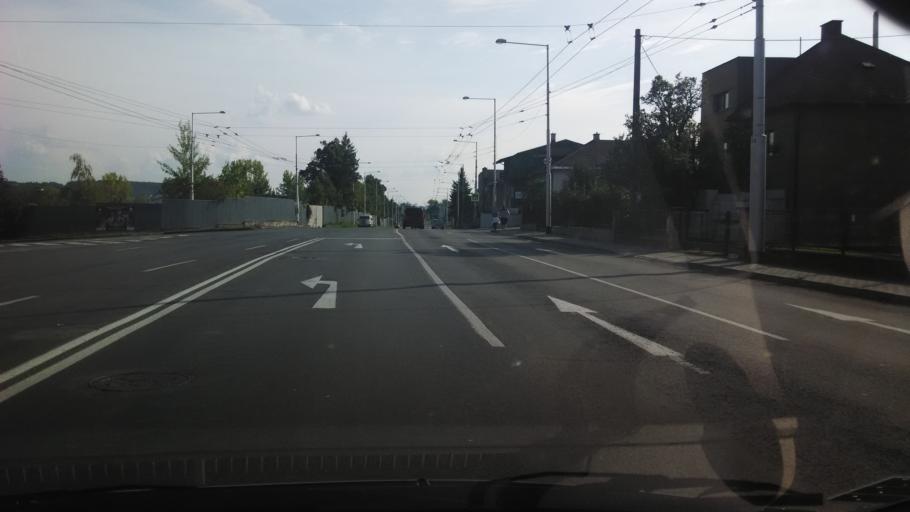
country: SK
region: Banskobystricky
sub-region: Okres Banska Bystrica
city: Banska Bystrica
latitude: 48.7175
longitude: 19.1324
